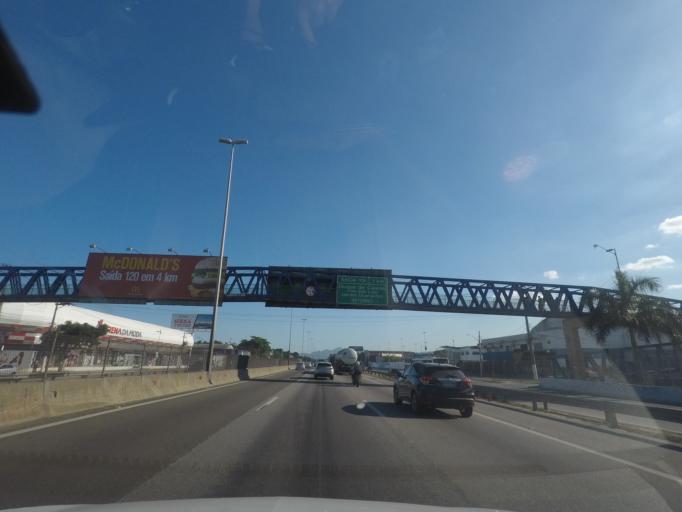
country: BR
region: Rio de Janeiro
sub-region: Duque De Caxias
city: Duque de Caxias
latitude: -22.7519
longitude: -43.2876
